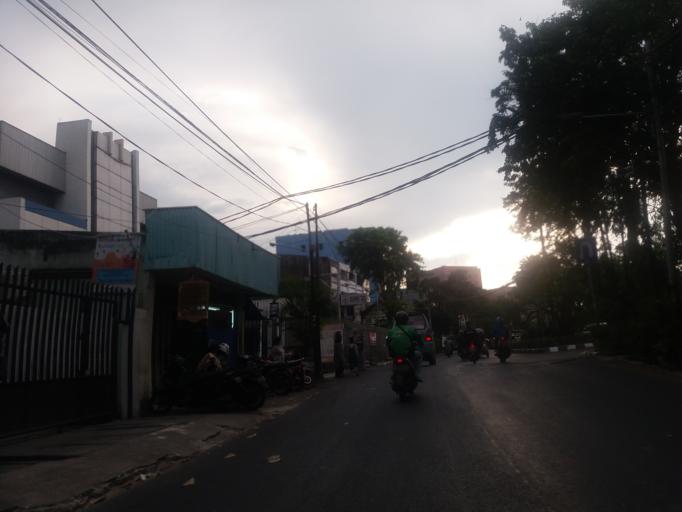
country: ID
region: Jakarta Raya
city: Jakarta
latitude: -6.1486
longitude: 106.8322
